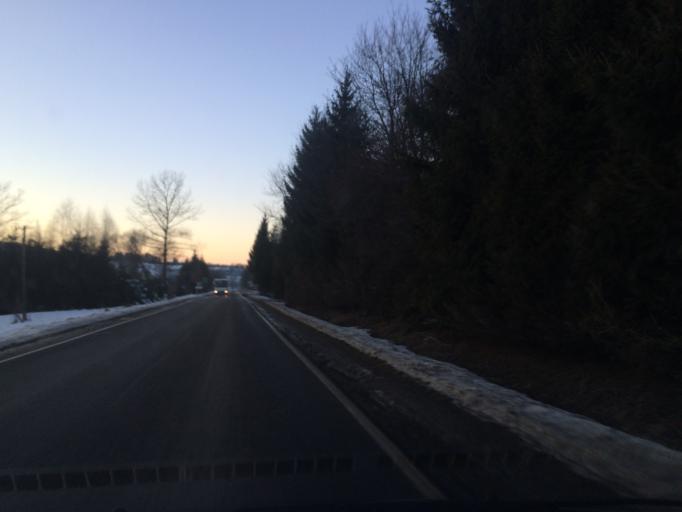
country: PL
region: Subcarpathian Voivodeship
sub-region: Powiat bieszczadzki
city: Czarna
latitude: 49.3709
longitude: 22.6516
